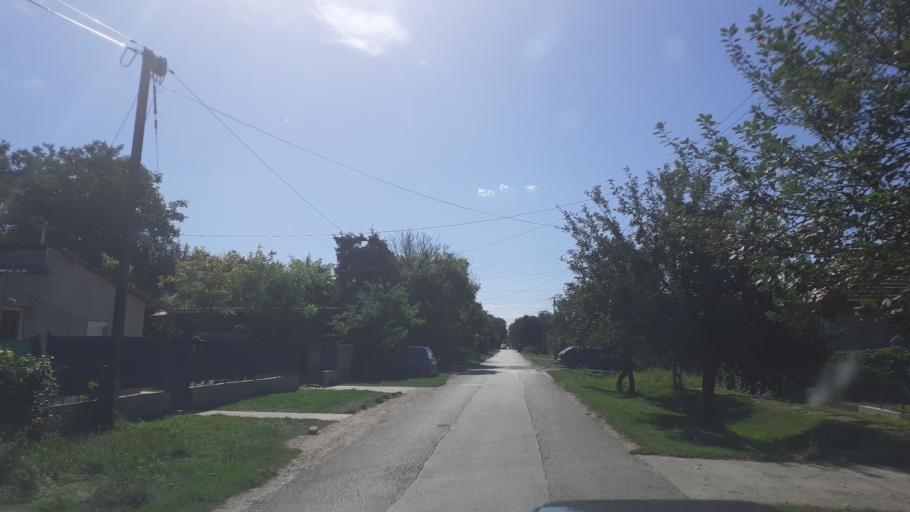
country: HU
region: Fejer
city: Baracska
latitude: 47.2817
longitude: 18.7709
